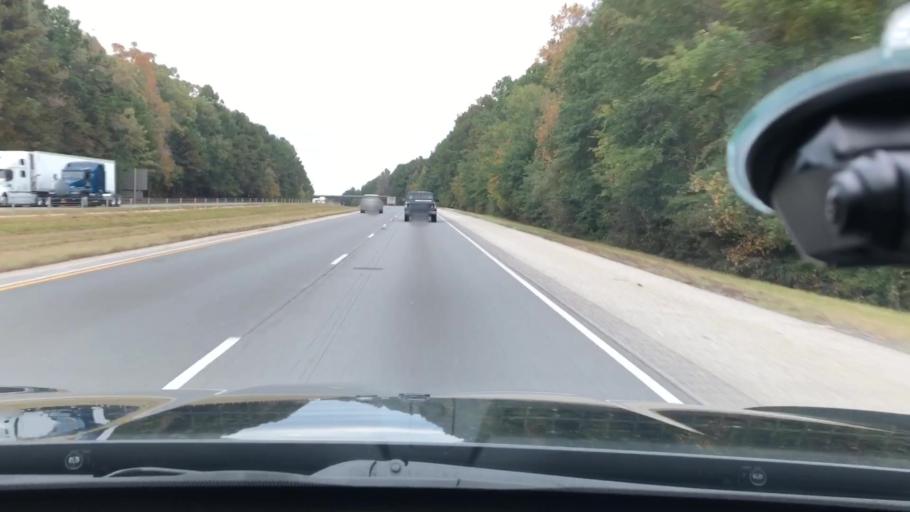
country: US
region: Arkansas
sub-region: Clark County
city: Arkadelphia
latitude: 34.1381
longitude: -93.0823
